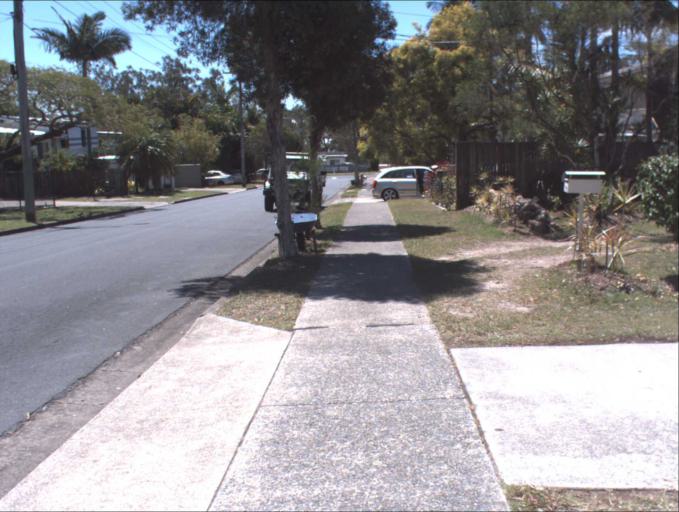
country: AU
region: Queensland
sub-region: Logan
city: Logan City
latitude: -27.6441
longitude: 153.1259
